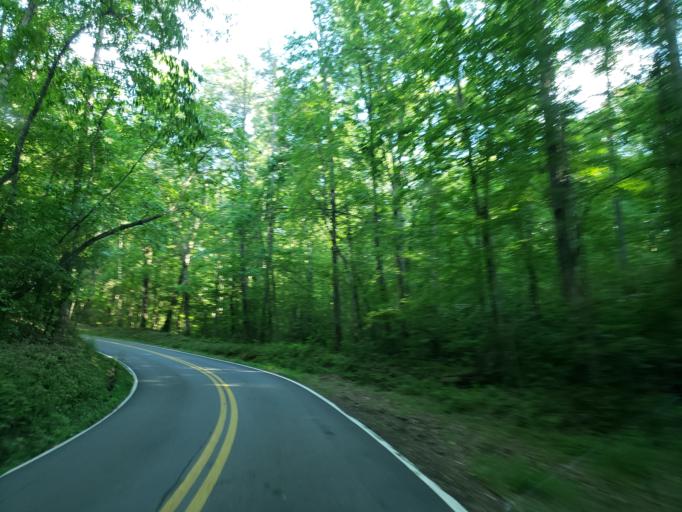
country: US
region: Georgia
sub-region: Murray County
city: Chatsworth
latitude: 34.6638
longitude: -84.6463
